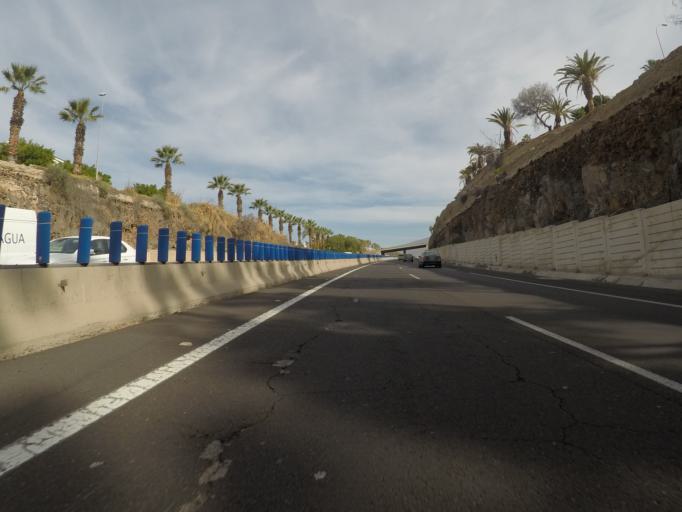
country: ES
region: Canary Islands
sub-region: Provincia de Santa Cruz de Tenerife
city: Playa de las Americas
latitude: 28.0749
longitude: -16.7292
